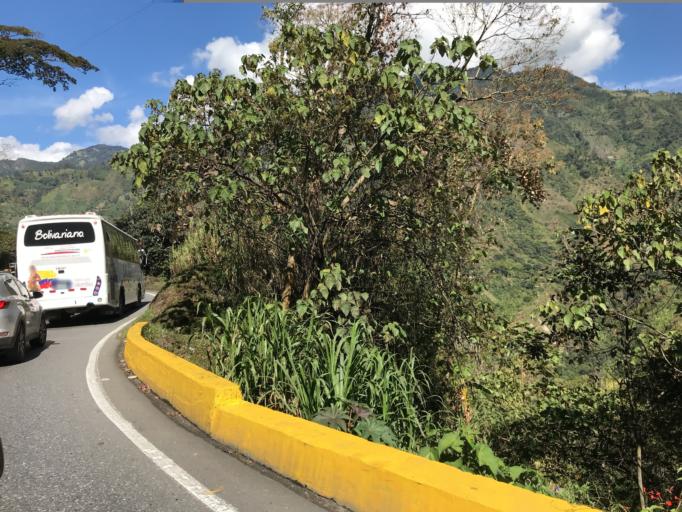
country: CO
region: Tolima
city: Cajamarca
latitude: 4.4425
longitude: -75.4120
